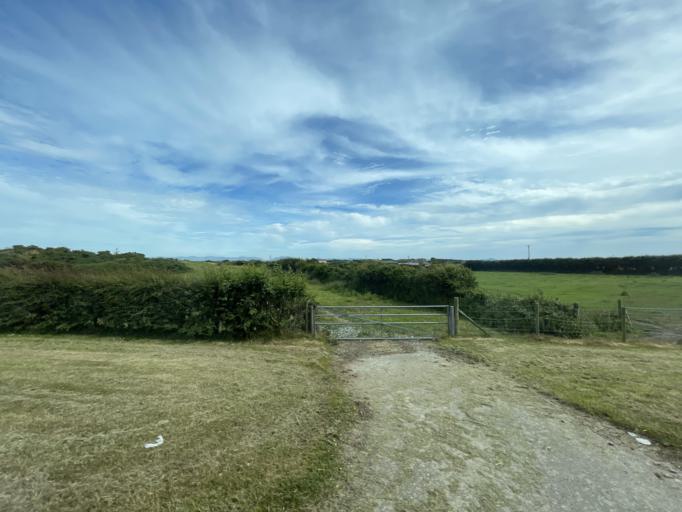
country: GB
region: Wales
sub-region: Anglesey
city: Valley
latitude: 53.2789
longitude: -4.5749
